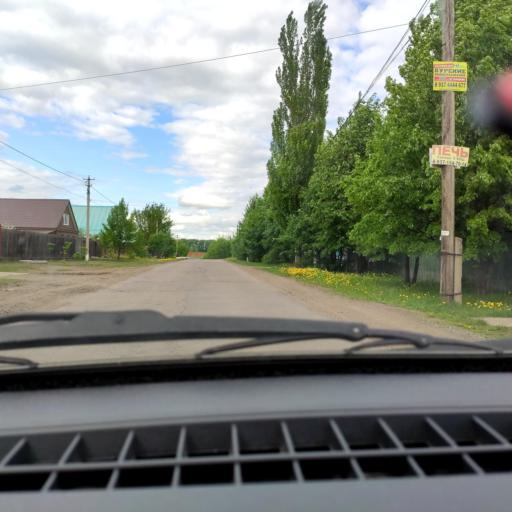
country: RU
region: Bashkortostan
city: Ufa
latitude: 54.5417
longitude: 55.9187
